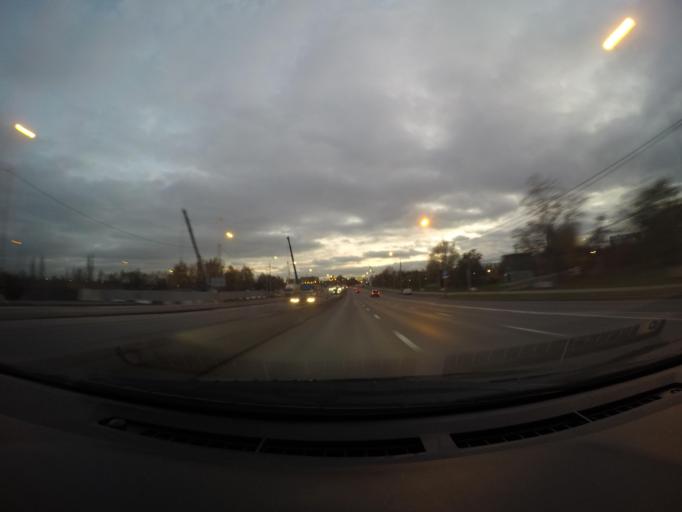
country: RU
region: Moscow
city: Kolomenskoye
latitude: 55.6625
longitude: 37.6565
